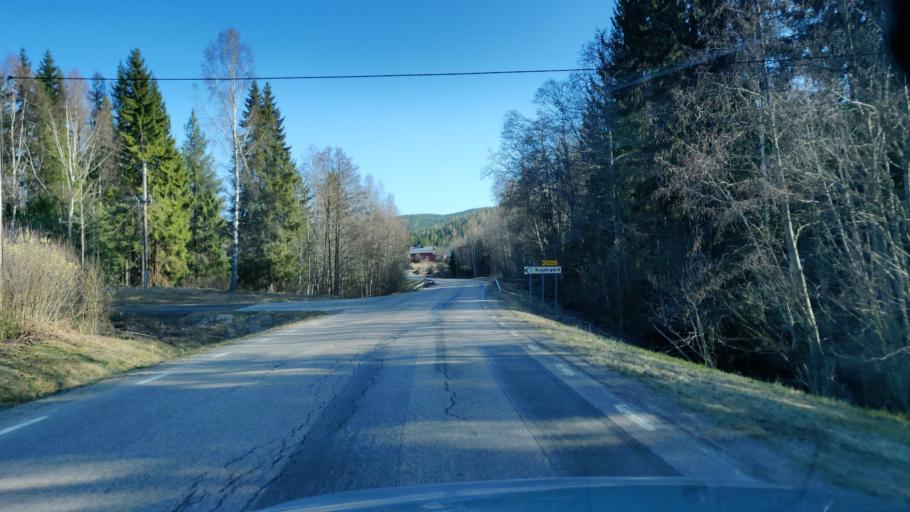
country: SE
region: Vaermland
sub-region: Munkfors Kommun
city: Munkfors
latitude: 59.9788
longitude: 13.4121
